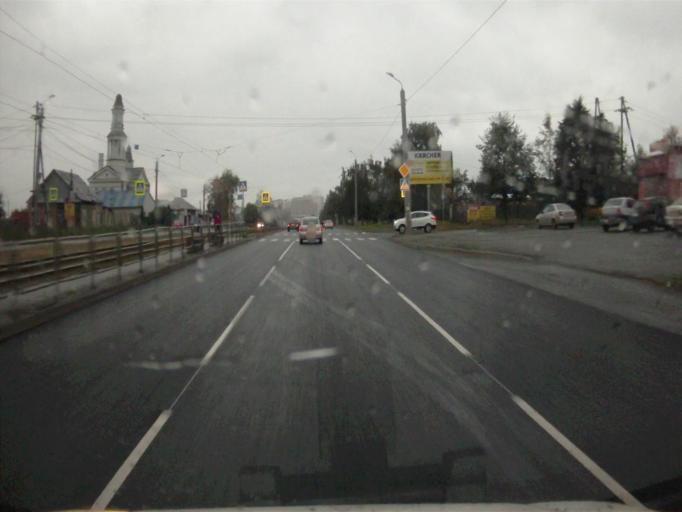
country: RU
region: Chelyabinsk
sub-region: Gorod Chelyabinsk
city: Chelyabinsk
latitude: 55.1849
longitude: 61.3686
